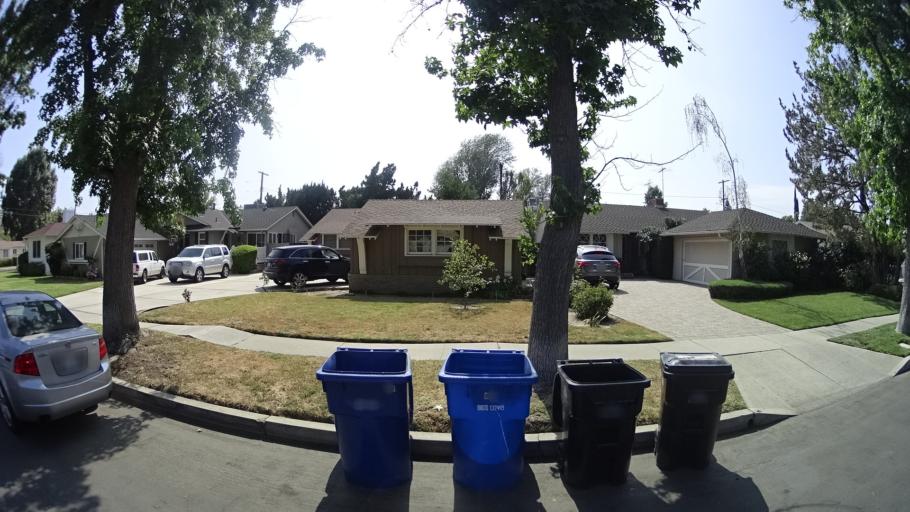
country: US
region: California
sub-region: Los Angeles County
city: Sherman Oaks
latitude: 34.1690
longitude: -118.4597
